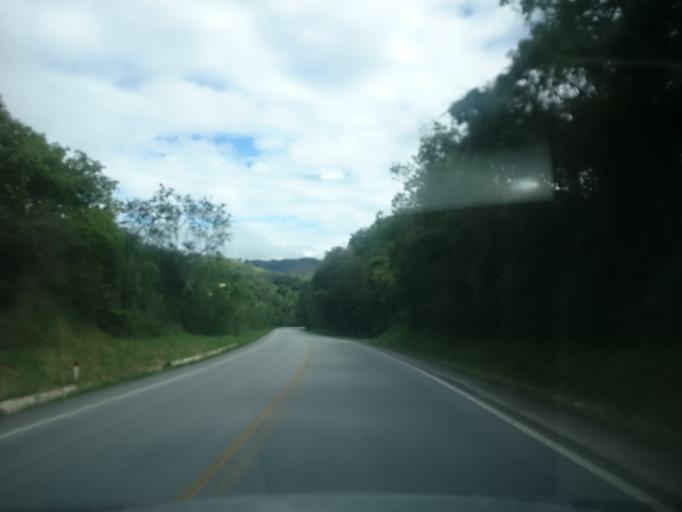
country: BR
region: Santa Catarina
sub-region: Anitapolis
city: Anitapolis
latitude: -27.7070
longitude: -49.2407
